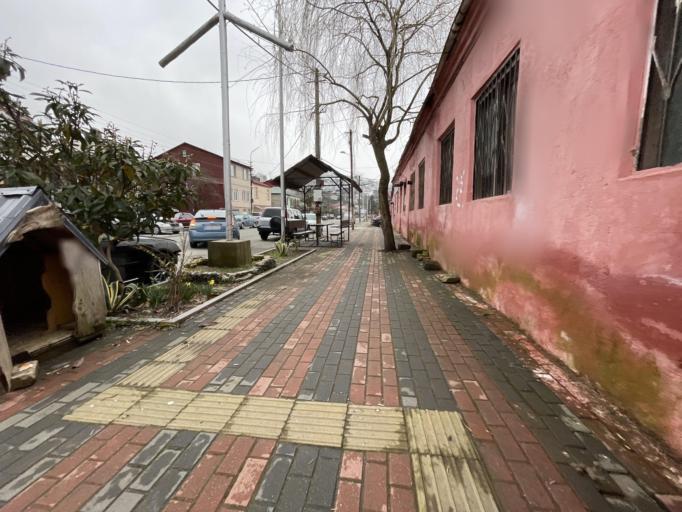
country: GE
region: Ajaria
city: Batumi
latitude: 41.6365
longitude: 41.6424
